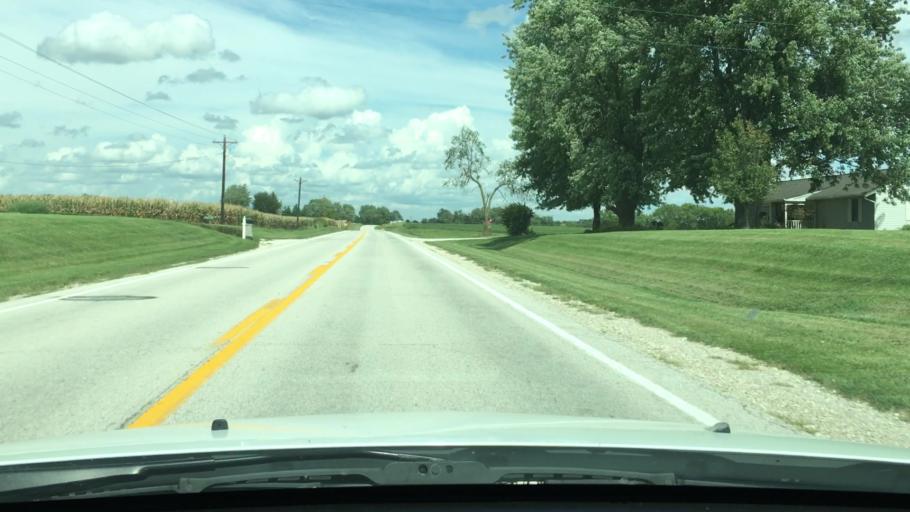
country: US
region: Illinois
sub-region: Pike County
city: Pittsfield
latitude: 39.5568
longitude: -90.9165
